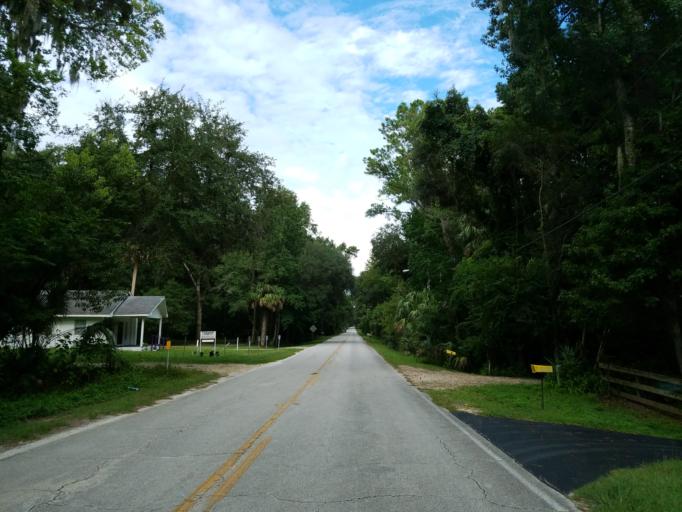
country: US
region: Florida
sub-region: Alachua County
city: Gainesville
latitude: 29.5033
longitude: -82.2773
